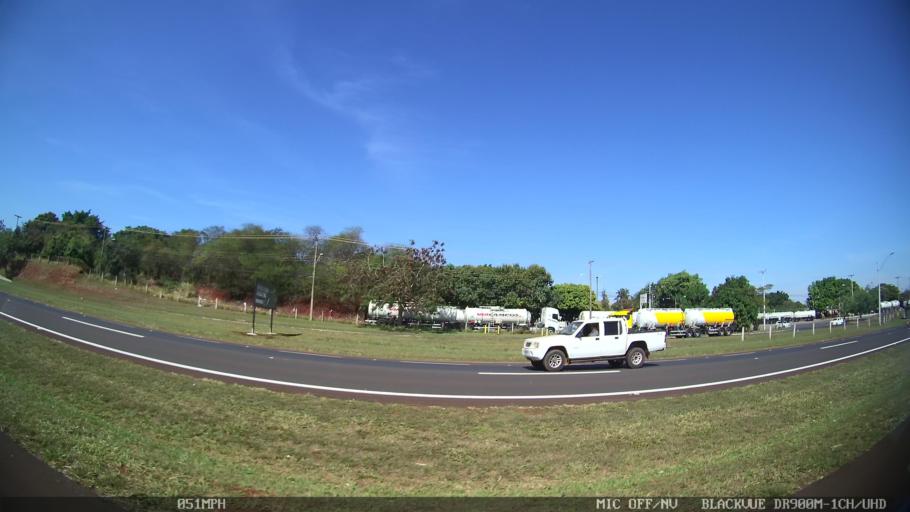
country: BR
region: Sao Paulo
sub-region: Ribeirao Preto
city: Ribeirao Preto
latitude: -21.1050
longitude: -47.8071
